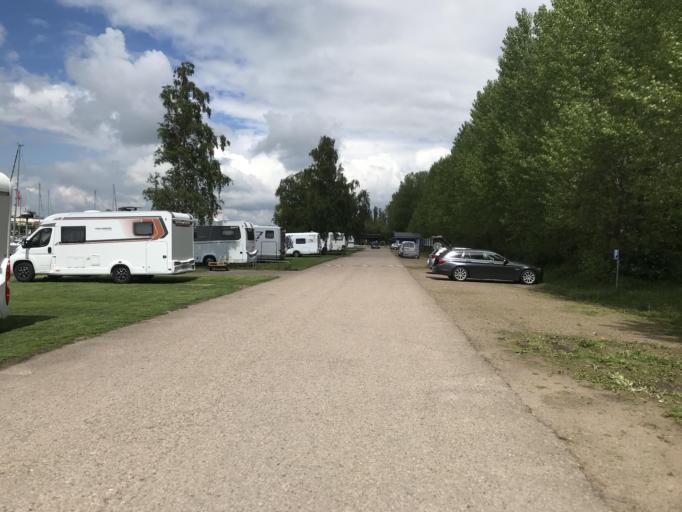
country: SE
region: Skane
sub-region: Landskrona
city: Landskrona
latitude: 55.8593
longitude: 12.8531
